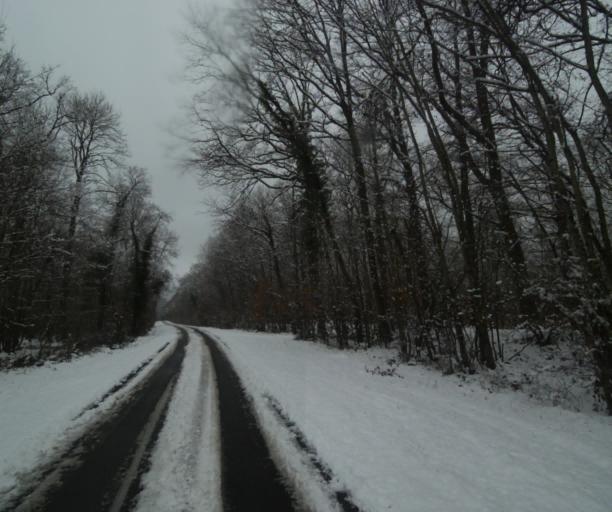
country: FR
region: Champagne-Ardenne
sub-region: Departement de la Haute-Marne
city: Wassy
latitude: 48.4685
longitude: 4.9526
